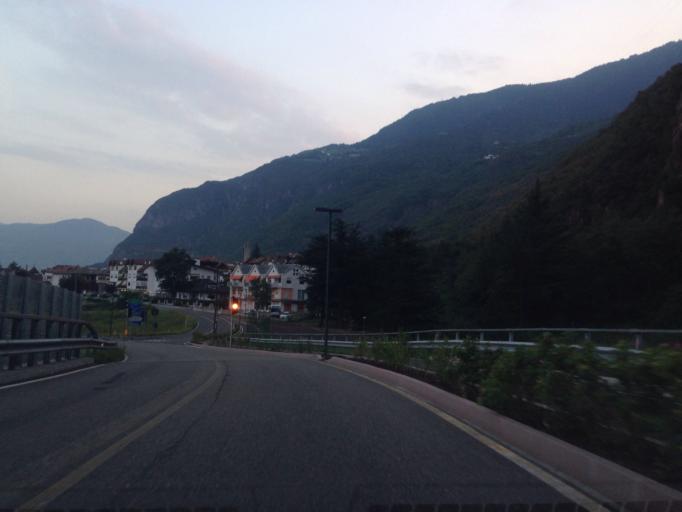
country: IT
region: Trentino-Alto Adige
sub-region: Bolzano
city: Pineta
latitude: 46.4342
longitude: 11.3469
